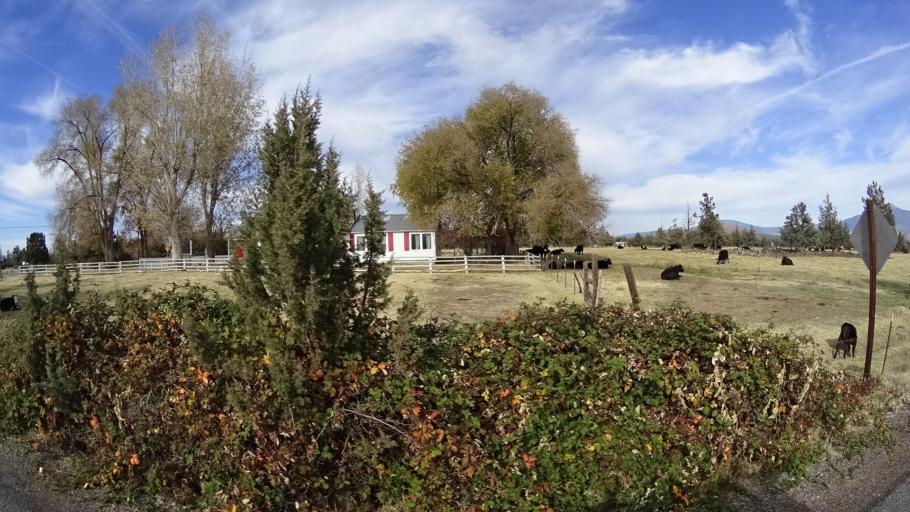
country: US
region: California
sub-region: Siskiyou County
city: Montague
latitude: 41.6385
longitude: -122.4182
